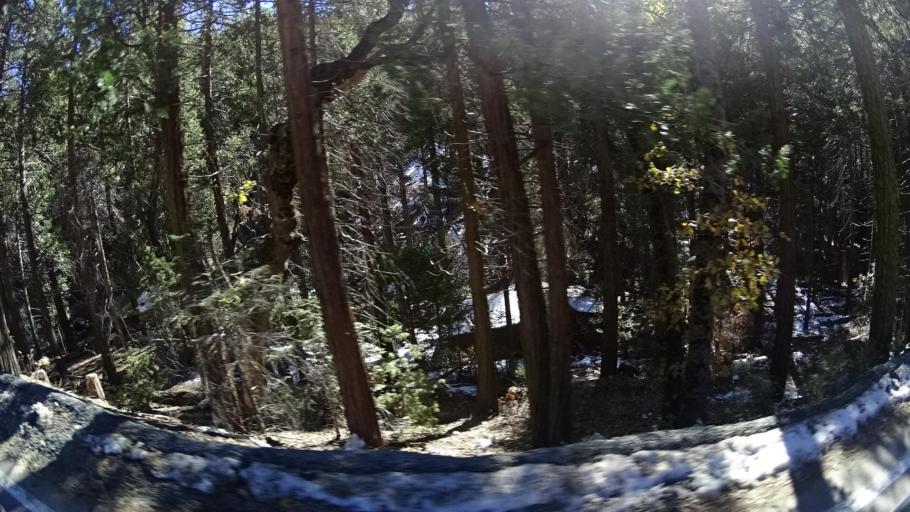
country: US
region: California
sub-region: Kern County
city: Alta Sierra
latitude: 35.7451
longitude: -118.5632
